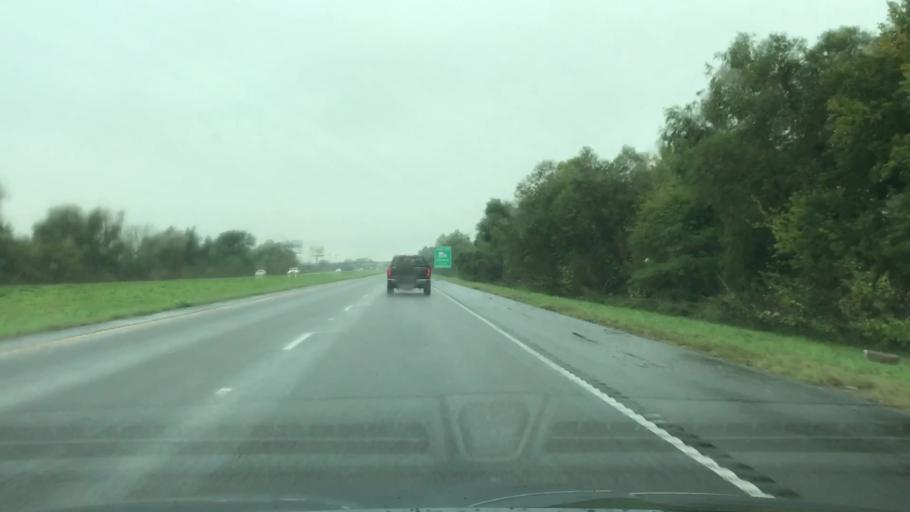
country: US
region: Louisiana
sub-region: Lafourche Parish
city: Raceland
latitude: 29.6900
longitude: -90.6140
